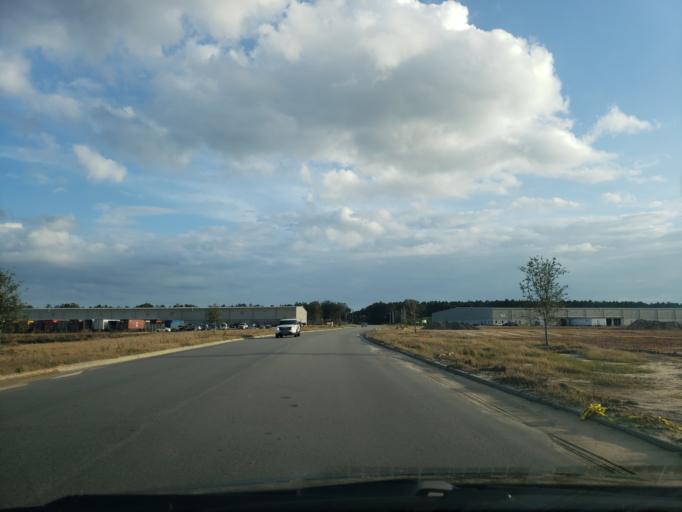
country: US
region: Georgia
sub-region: Chatham County
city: Bloomingdale
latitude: 32.1641
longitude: -81.2695
